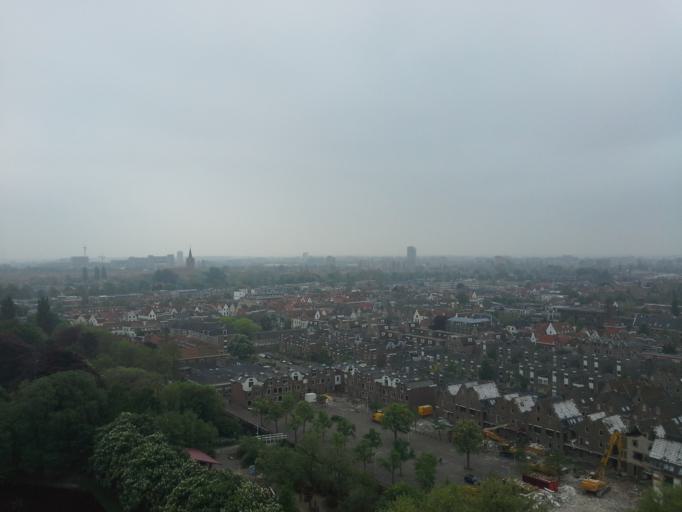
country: NL
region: South Holland
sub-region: Gemeente Leiden
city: Leiden
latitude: 52.1590
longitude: 4.5046
